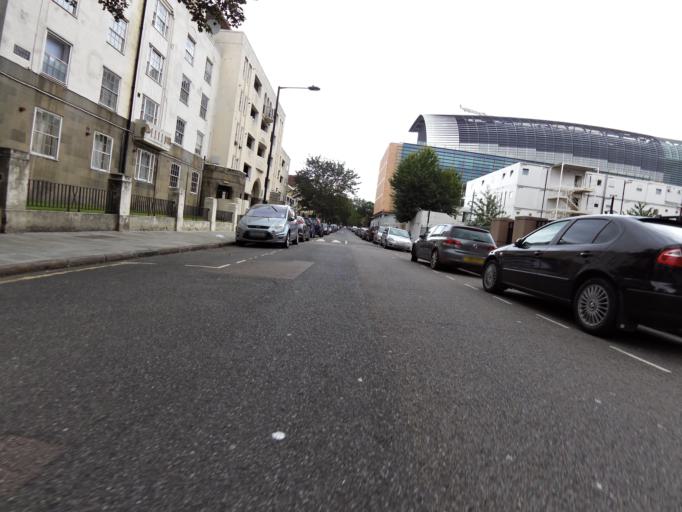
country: GB
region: England
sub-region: Greater London
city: Barnsbury
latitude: 51.5301
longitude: -0.1290
